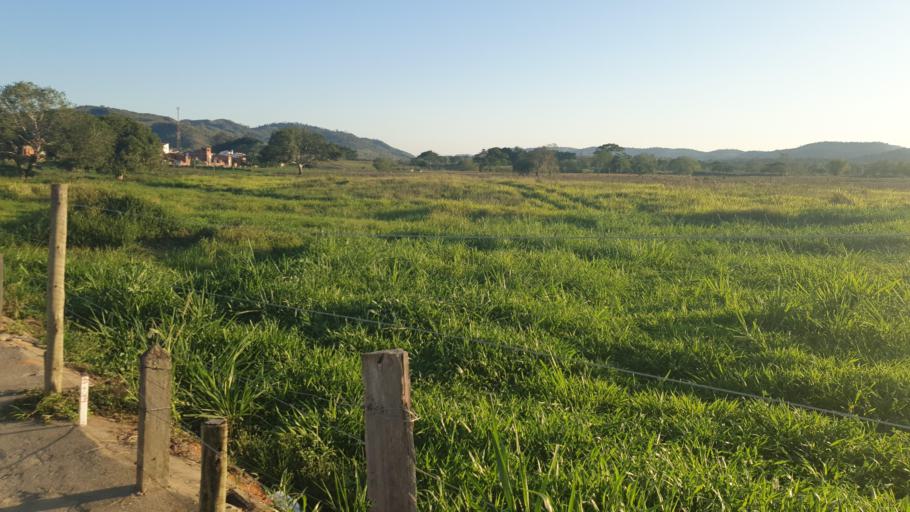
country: BR
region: Bahia
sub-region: Itagiba
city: Itagiba
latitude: -14.4280
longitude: -39.9051
